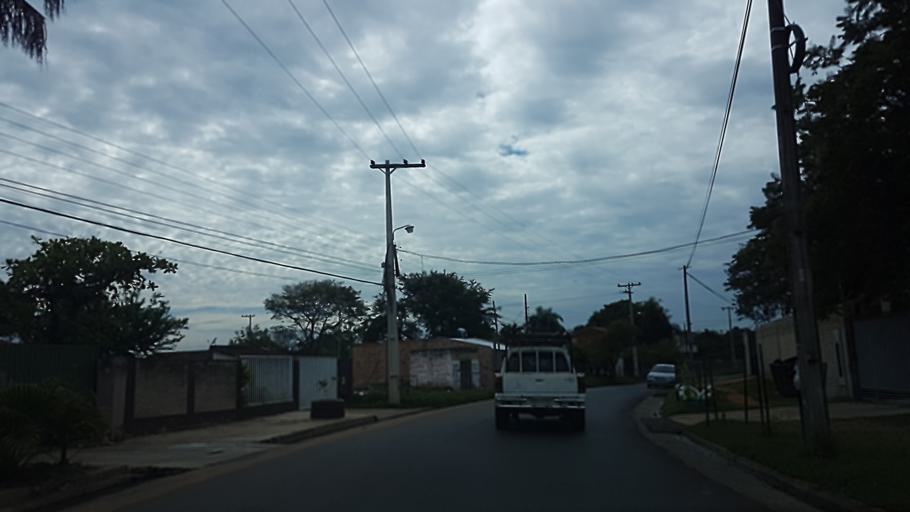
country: PY
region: Central
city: Colonia Mariano Roque Alonso
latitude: -25.2202
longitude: -57.5263
